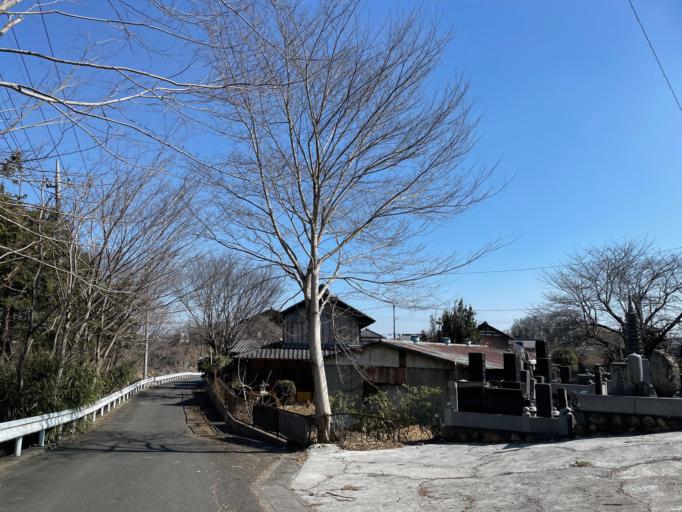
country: JP
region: Saitama
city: Yorii
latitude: 36.1187
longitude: 139.2066
